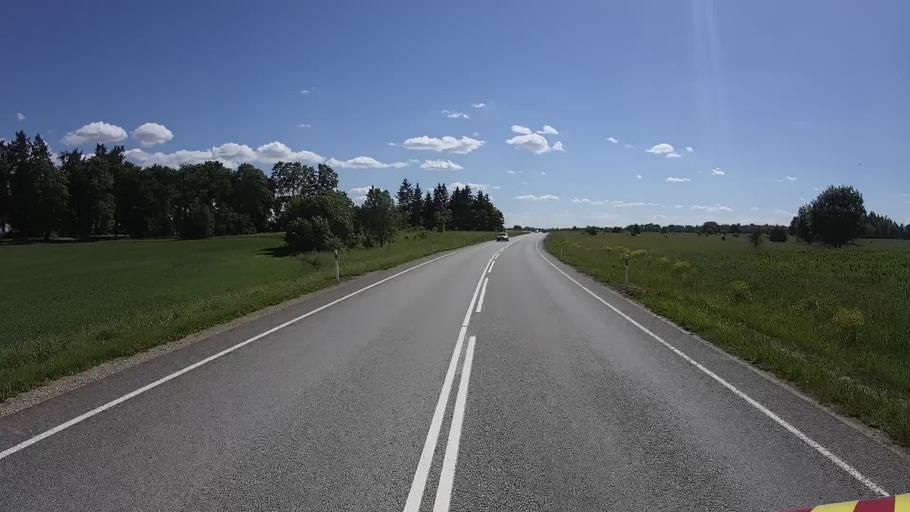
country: EE
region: Ida-Virumaa
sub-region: Johvi vald
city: Johvi
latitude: 59.3780
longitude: 27.3512
